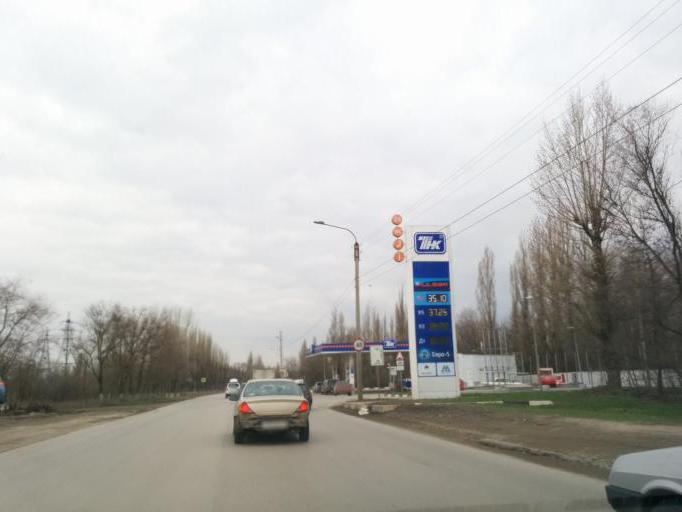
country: RU
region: Rostov
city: Novocherkassk
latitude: 47.4817
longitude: 40.1029
